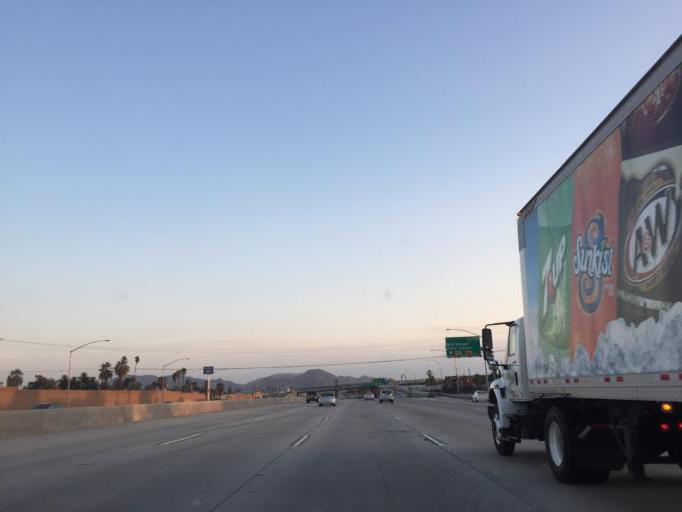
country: US
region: California
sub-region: San Bernardino County
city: San Bernardino
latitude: 34.1133
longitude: -117.3028
